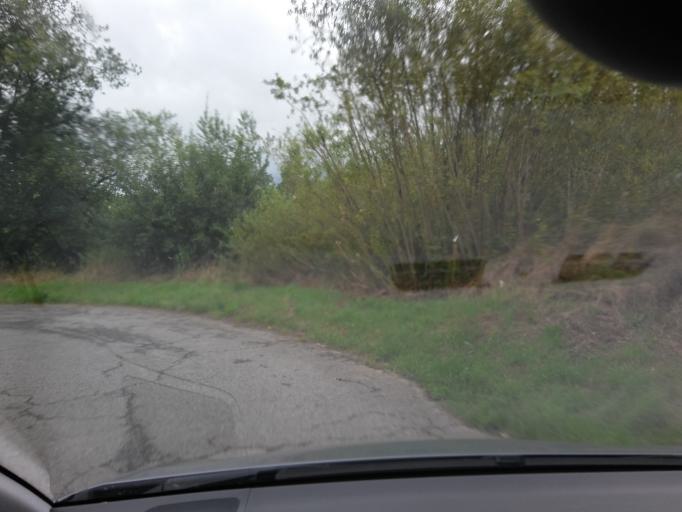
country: BE
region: Wallonia
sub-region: Province du Luxembourg
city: Arlon
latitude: 49.6808
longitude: 5.8003
